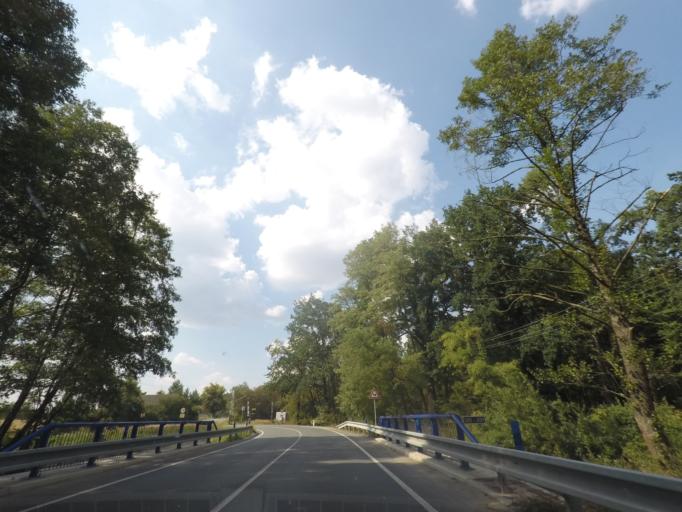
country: CZ
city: Albrechtice nad Orlici
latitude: 50.1293
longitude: 16.0640
